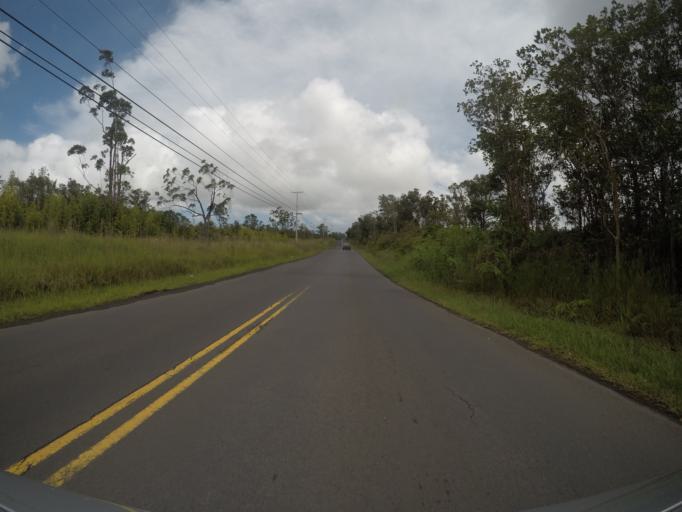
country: US
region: Hawaii
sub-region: Hawaii County
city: Fern Acres
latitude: 19.4798
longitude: -155.1427
